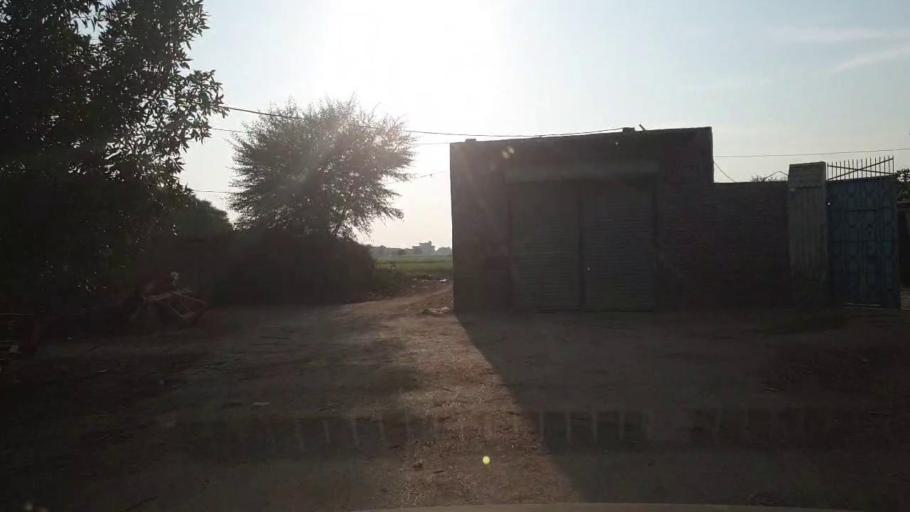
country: PK
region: Sindh
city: Shahpur Chakar
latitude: 26.1493
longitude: 68.6330
